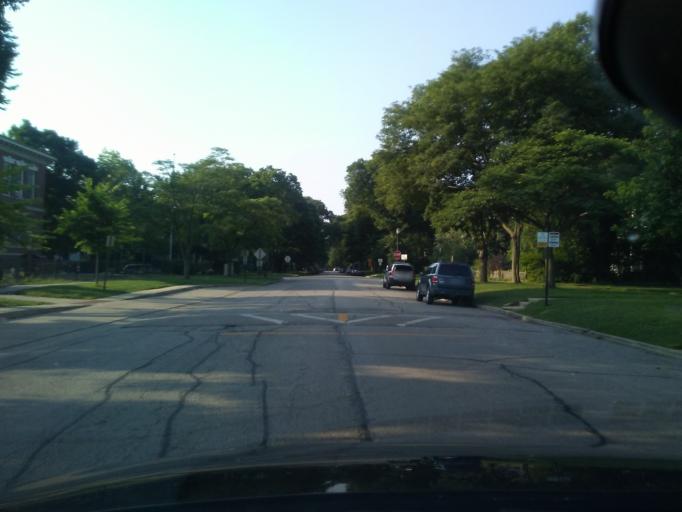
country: US
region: Illinois
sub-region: Cook County
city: Evanston
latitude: 42.0419
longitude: -87.6788
